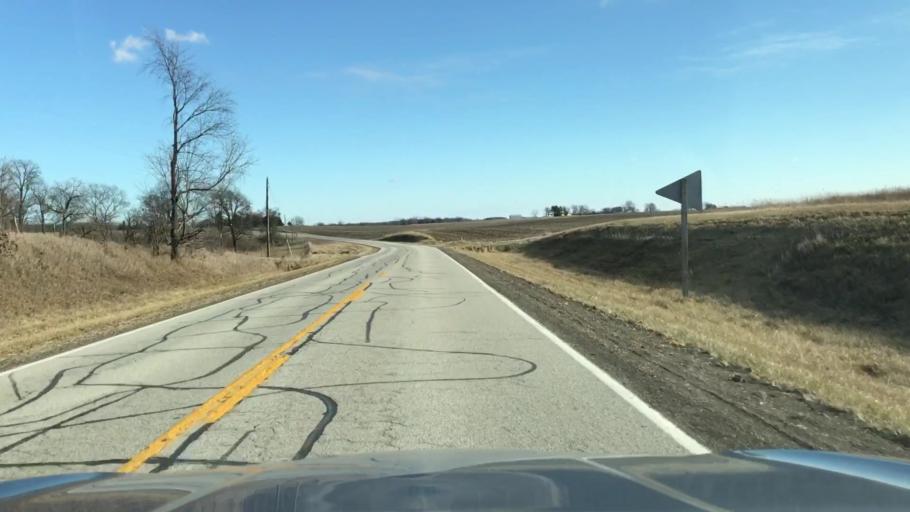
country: US
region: Illinois
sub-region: McLean County
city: Lexington
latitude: 40.6495
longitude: -88.8760
